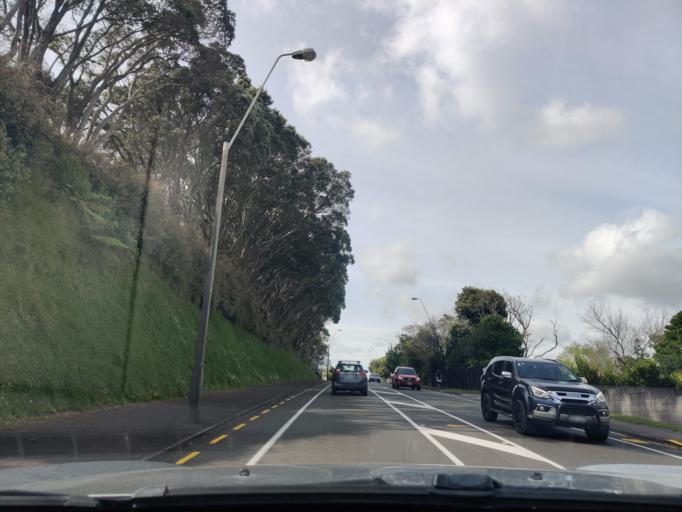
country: NZ
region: Taranaki
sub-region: New Plymouth District
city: New Plymouth
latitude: -39.0593
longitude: 174.0849
